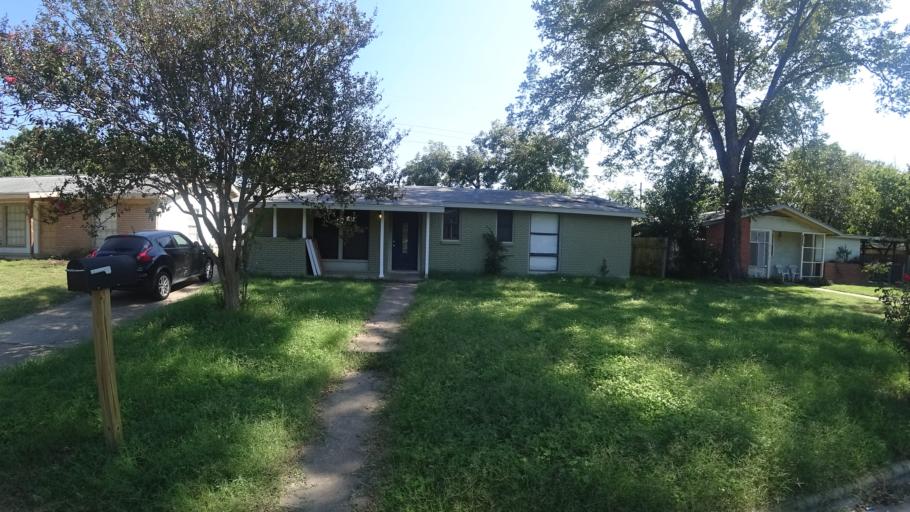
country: US
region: Texas
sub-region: Travis County
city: Austin
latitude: 30.3141
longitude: -97.6856
